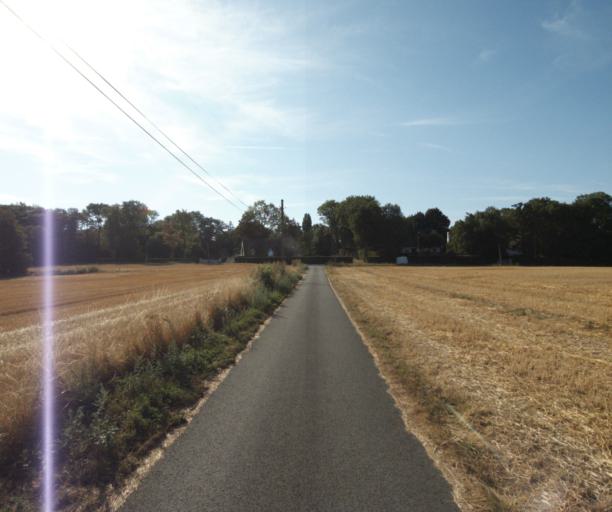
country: FR
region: Nord-Pas-de-Calais
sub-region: Departement du Nord
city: Roncq
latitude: 50.7653
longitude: 3.1408
